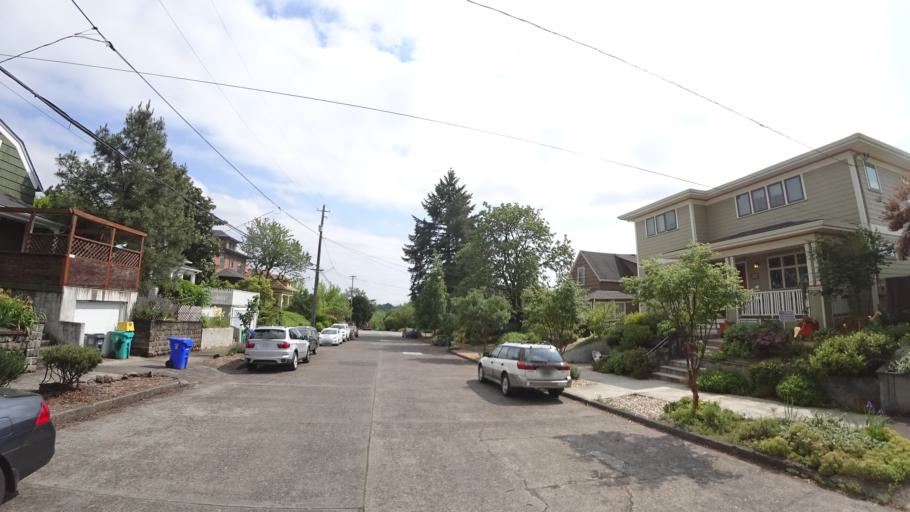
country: US
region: Oregon
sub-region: Multnomah County
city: Portland
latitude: 45.5550
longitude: -122.6493
